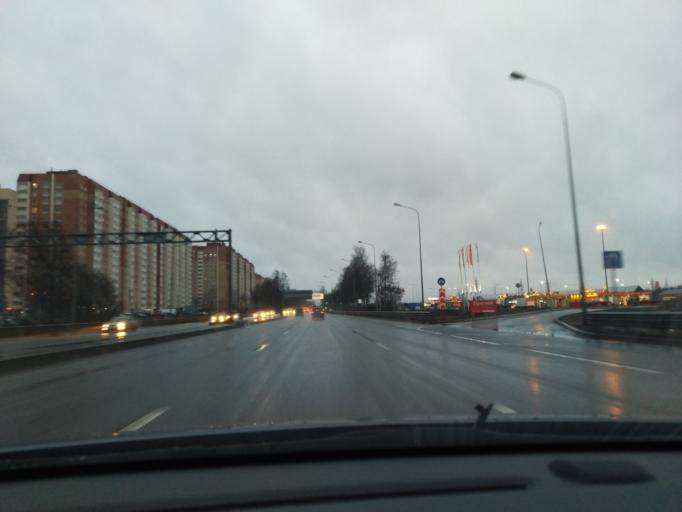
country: RU
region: St.-Petersburg
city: Gorelovo
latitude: 59.7958
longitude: 30.1517
